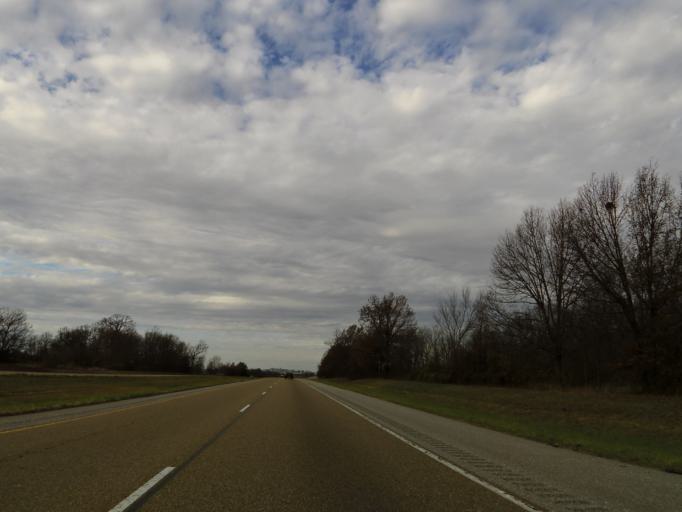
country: US
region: Illinois
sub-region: Clinton County
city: Wamac
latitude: 38.3892
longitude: -89.2107
